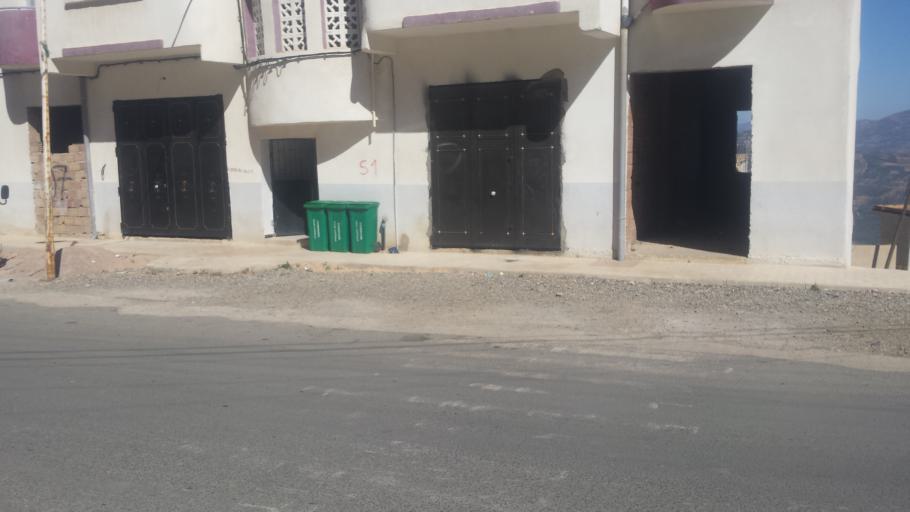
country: DZ
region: Tizi Ouzou
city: Chemini
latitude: 36.6054
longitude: 4.6388
